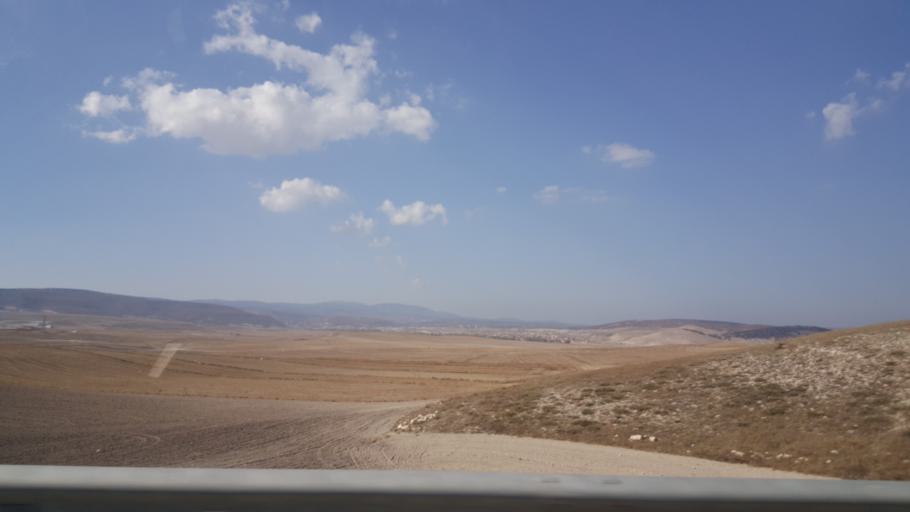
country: TR
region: Eskisehir
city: Kirka
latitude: 39.3114
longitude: 30.5387
